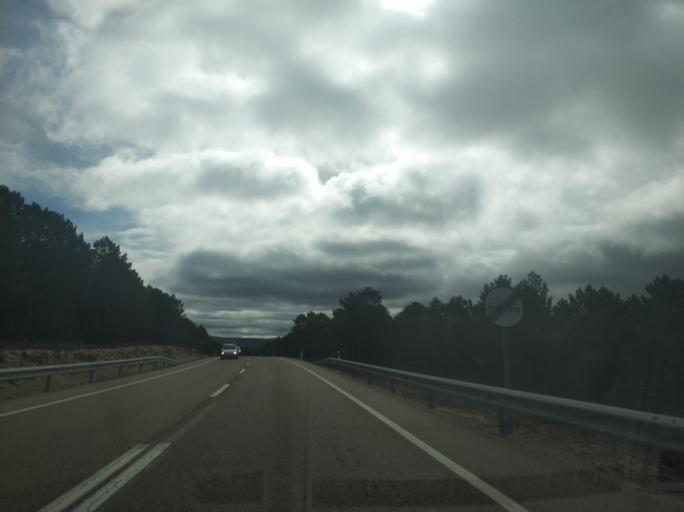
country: ES
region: Castille and Leon
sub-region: Provincia de Soria
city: Muriel Viejo
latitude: 41.8176
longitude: -2.9189
